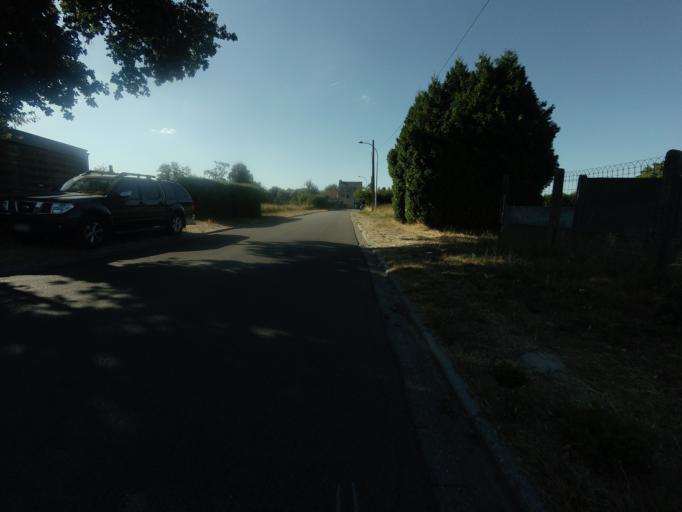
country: BE
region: Flanders
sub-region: Provincie Antwerpen
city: Beerse
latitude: 51.3275
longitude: 4.8708
